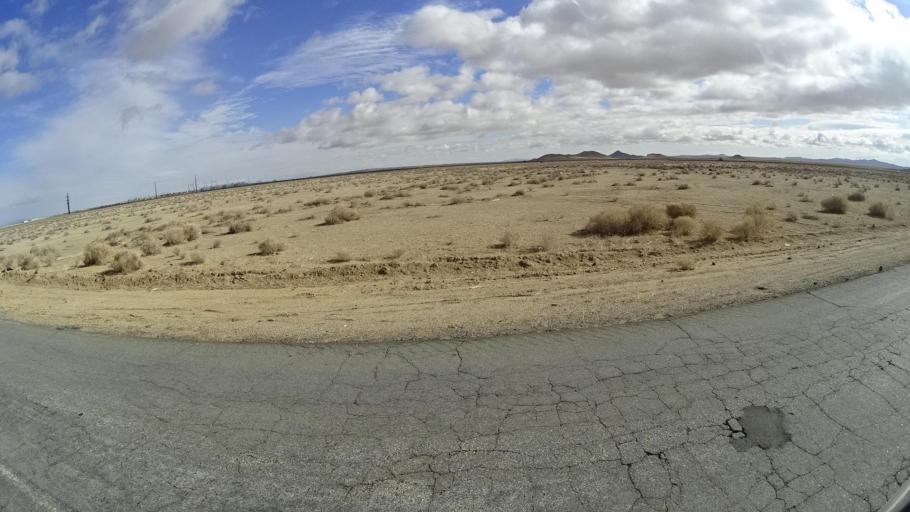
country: US
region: California
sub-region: Kern County
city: Mojave
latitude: 35.0207
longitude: -118.1497
